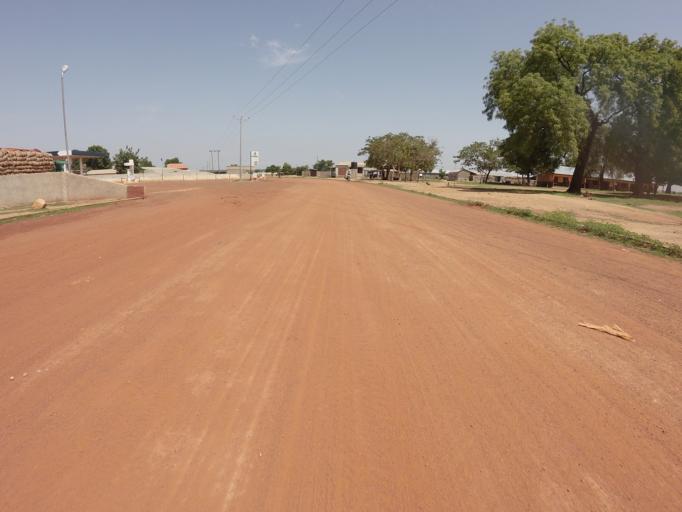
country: GH
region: Upper East
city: Bawku
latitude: 11.1450
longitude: -0.2086
